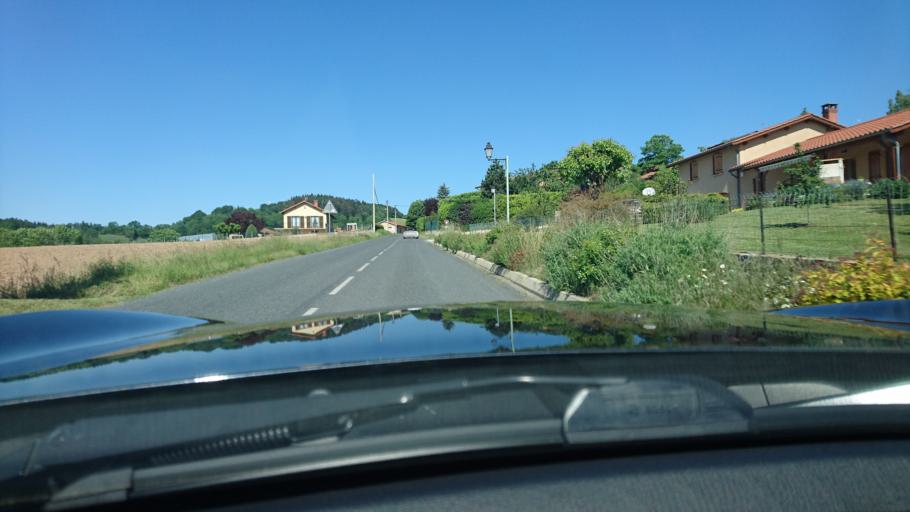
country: FR
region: Rhone-Alpes
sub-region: Departement du Rhone
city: Montrottier
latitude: 45.7945
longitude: 4.4626
